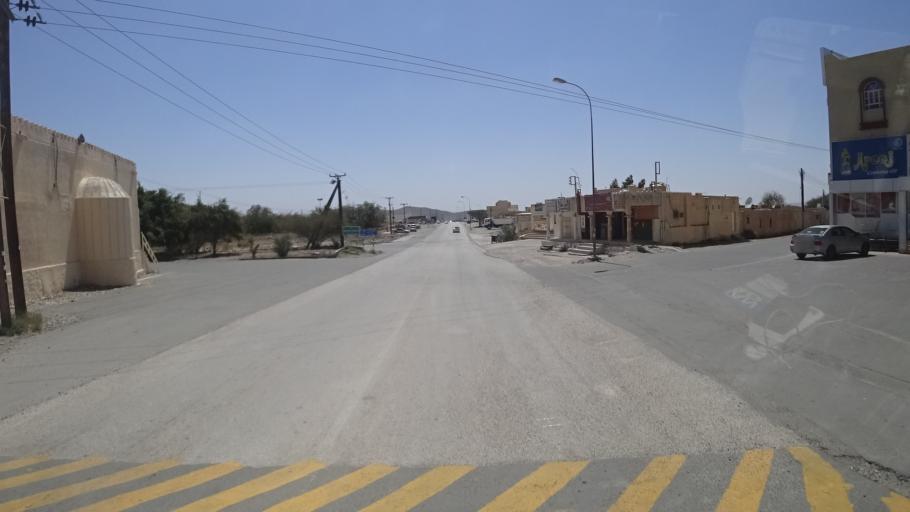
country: OM
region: Az Zahirah
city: `Ibri
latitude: 23.1325
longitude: 56.8905
